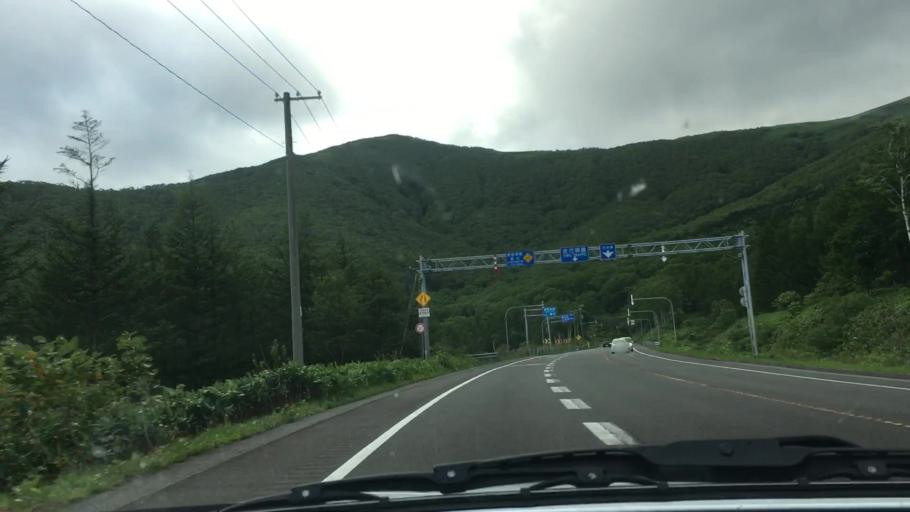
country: JP
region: Hokkaido
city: Shimo-furano
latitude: 43.1571
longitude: 142.7832
